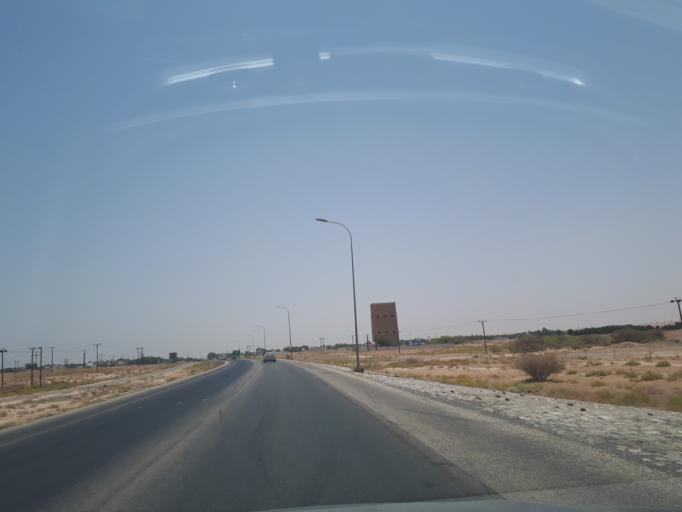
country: OM
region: Ash Sharqiyah
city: Al Qabil
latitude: 22.5109
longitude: 58.7399
